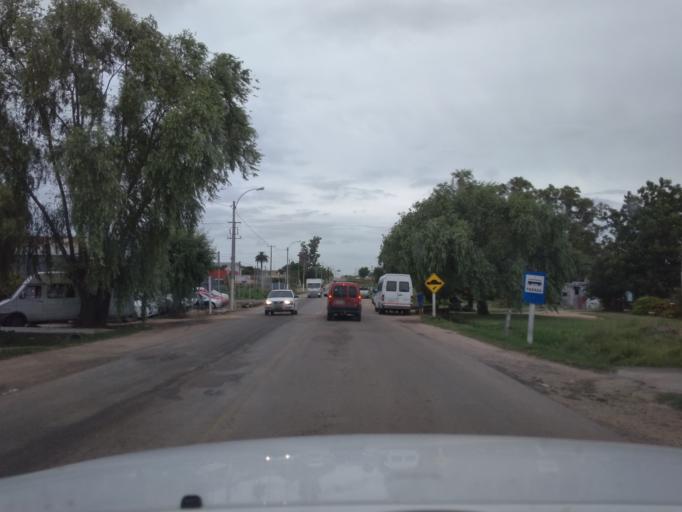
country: UY
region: Canelones
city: Tala
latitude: -34.3470
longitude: -55.7657
